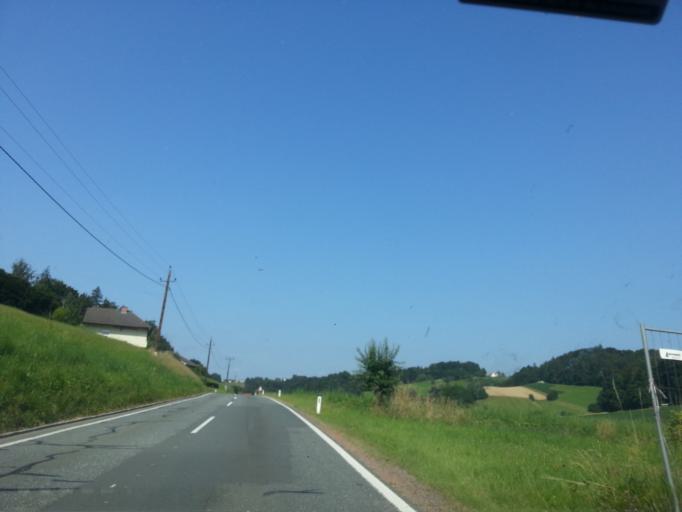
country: AT
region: Styria
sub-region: Politischer Bezirk Leibnitz
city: Grossklein
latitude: 46.7347
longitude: 15.4534
